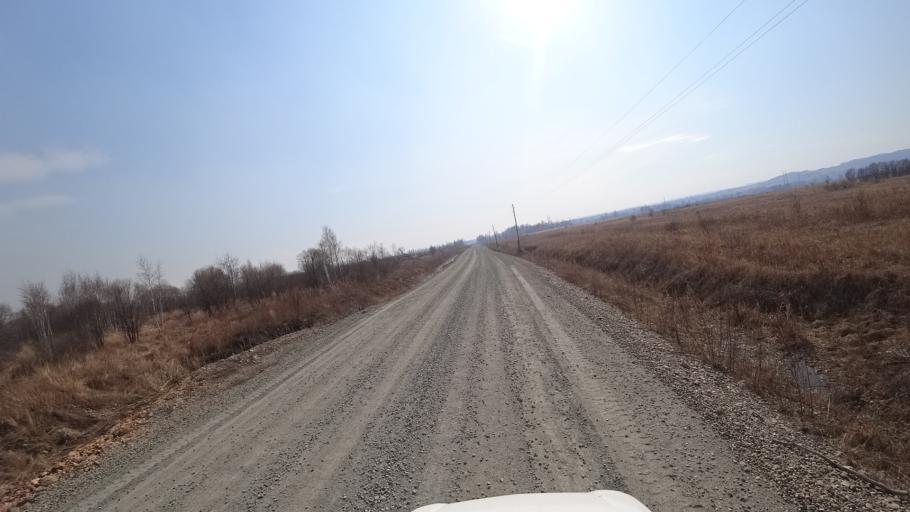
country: RU
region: Amur
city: Novobureyskiy
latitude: 49.8094
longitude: 129.9678
